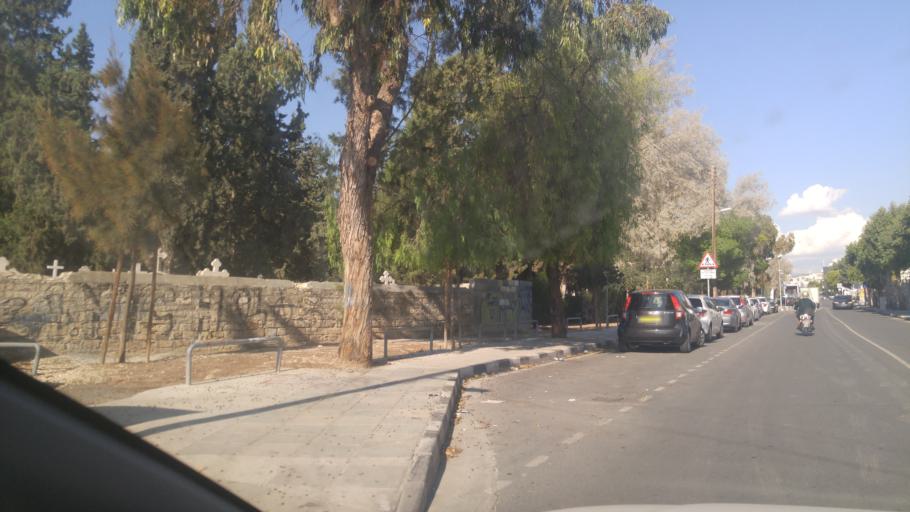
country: CY
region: Limassol
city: Limassol
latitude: 34.6905
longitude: 33.0578
